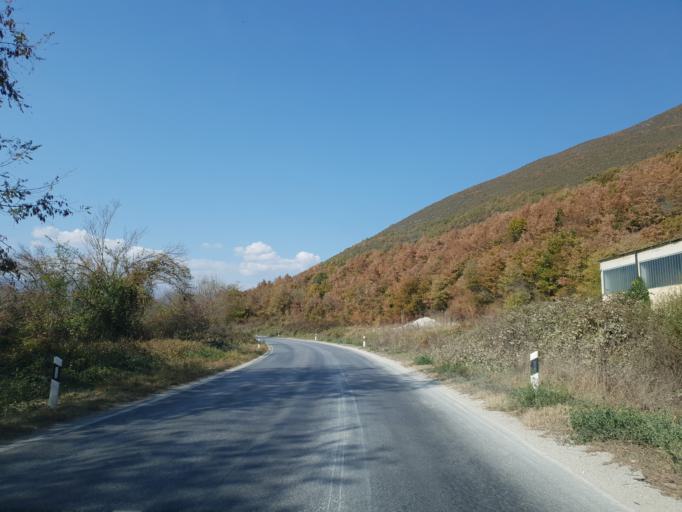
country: MK
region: Vranestica
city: Vranestica
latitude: 41.4726
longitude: 21.0097
